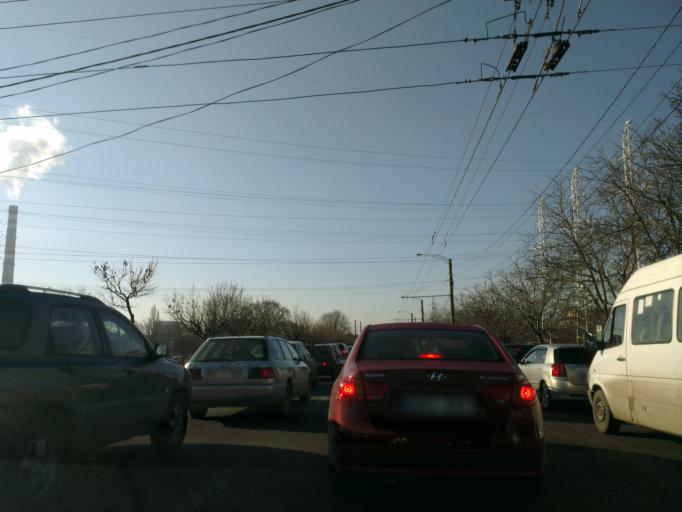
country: MD
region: Chisinau
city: Chisinau
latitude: 47.0343
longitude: 28.8890
